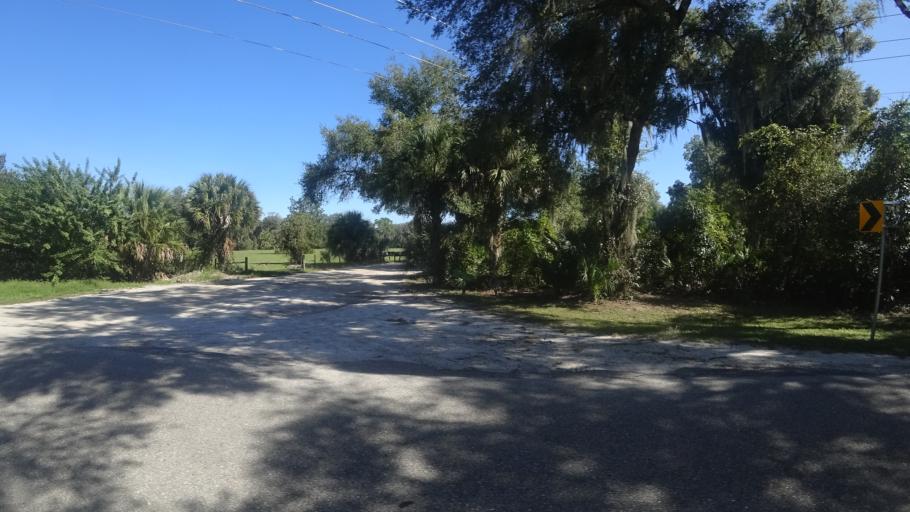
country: US
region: Florida
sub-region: Sarasota County
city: Lake Sarasota
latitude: 27.3203
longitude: -82.2672
